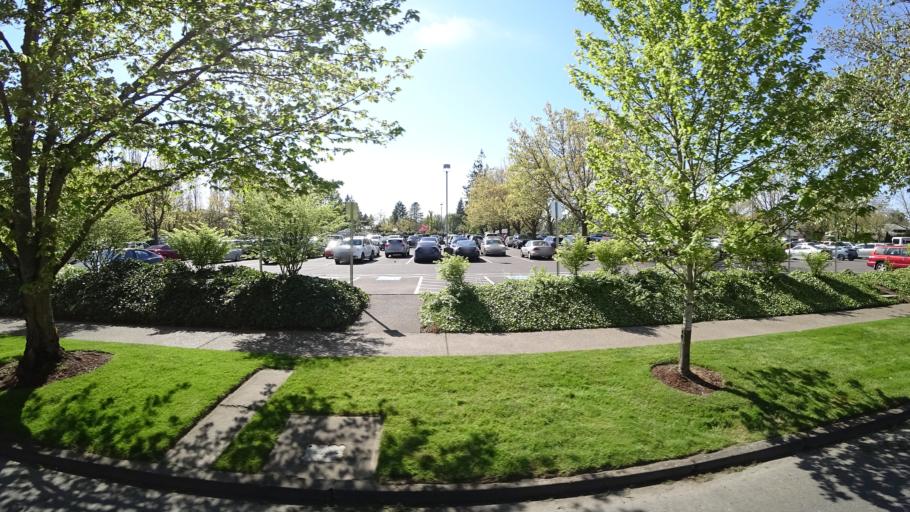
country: US
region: Oregon
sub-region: Washington County
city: Hillsboro
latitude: 45.5245
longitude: -122.9898
